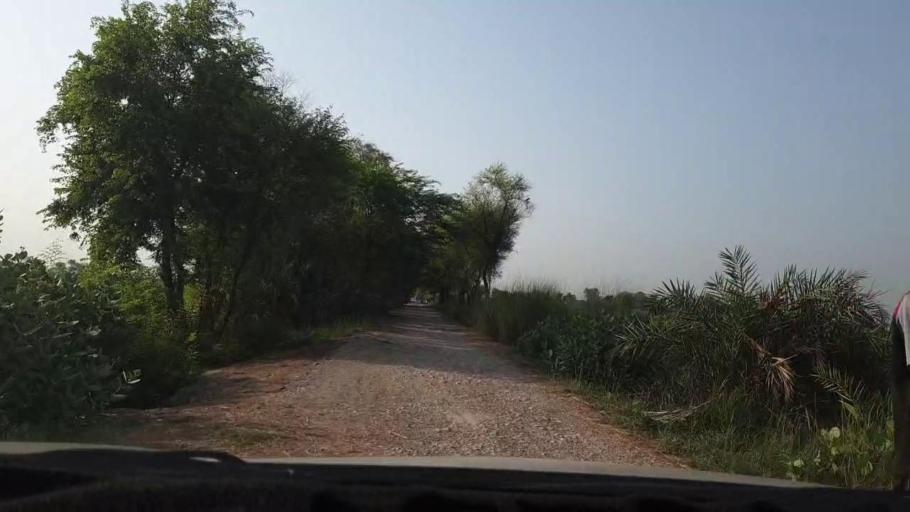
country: PK
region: Sindh
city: Larkana
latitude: 27.5055
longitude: 68.1742
